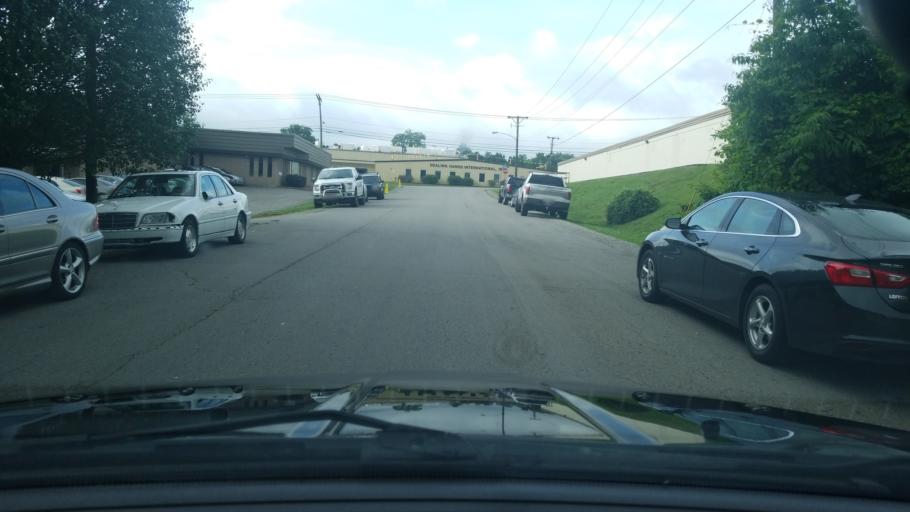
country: US
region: Tennessee
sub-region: Davidson County
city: Oak Hill
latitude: 36.0936
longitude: -86.7429
